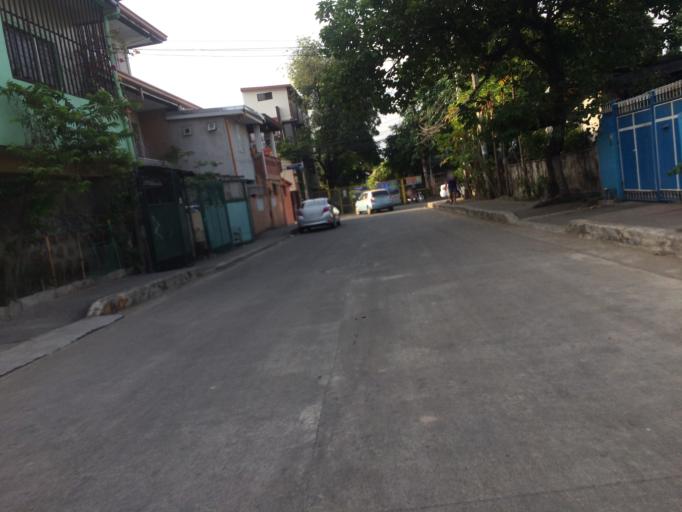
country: PH
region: Calabarzon
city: Bagong Pagasa
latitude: 14.6726
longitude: 121.0186
